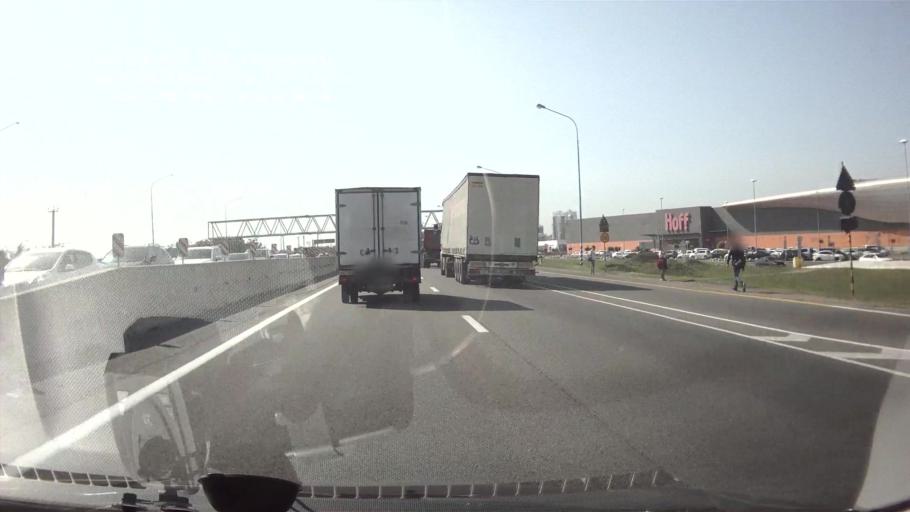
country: RU
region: Krasnodarskiy
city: Pashkovskiy
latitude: 45.0097
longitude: 39.1262
